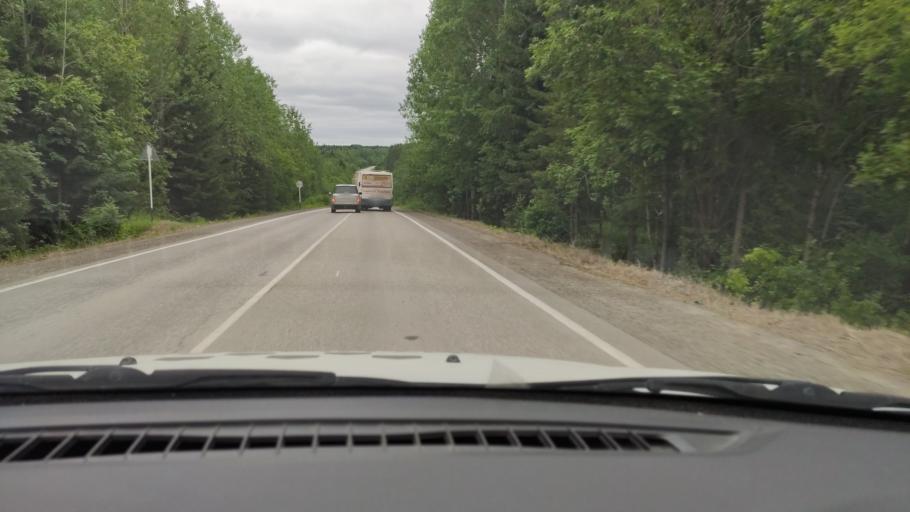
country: RU
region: Perm
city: Novyye Lyady
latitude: 58.0266
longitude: 56.6772
